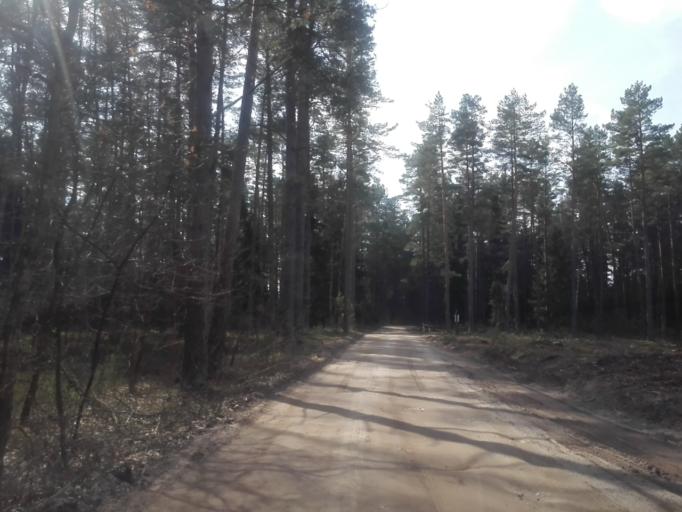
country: PL
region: Podlasie
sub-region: Powiat sejnenski
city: Sejny
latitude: 54.0248
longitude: 23.4090
